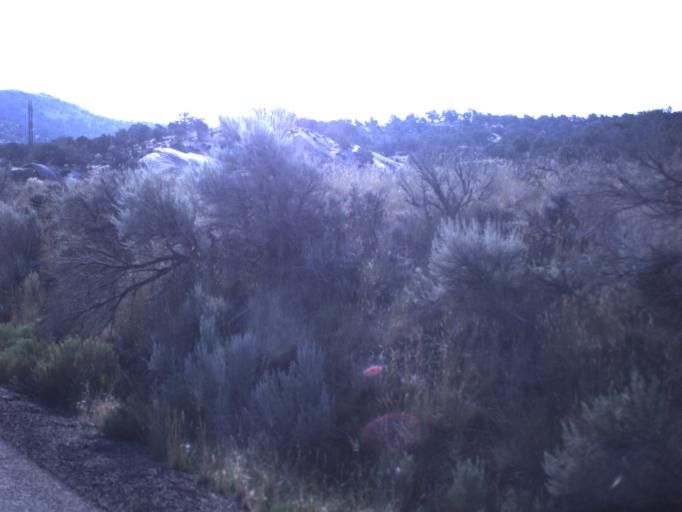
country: US
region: Utah
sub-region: Uintah County
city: Vernal
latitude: 40.5834
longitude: -109.4725
